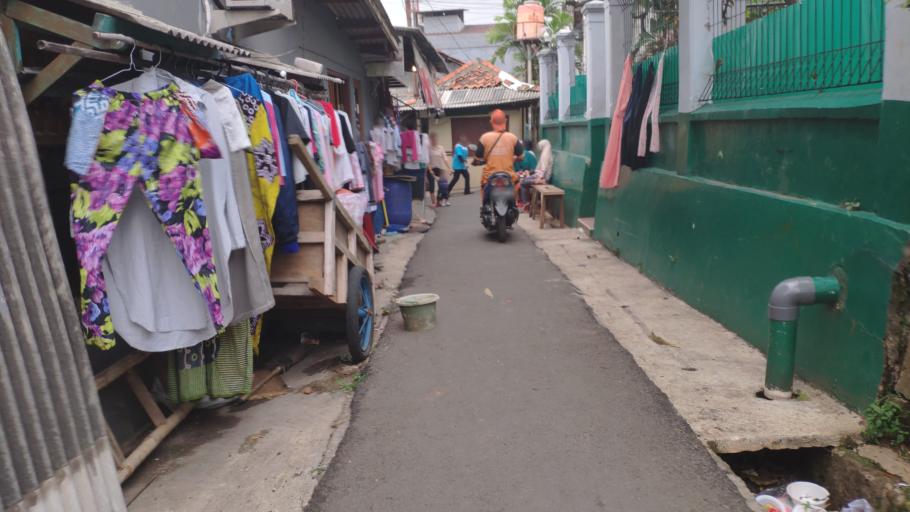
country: ID
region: Jakarta Raya
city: Jakarta
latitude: -6.2710
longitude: 106.8295
